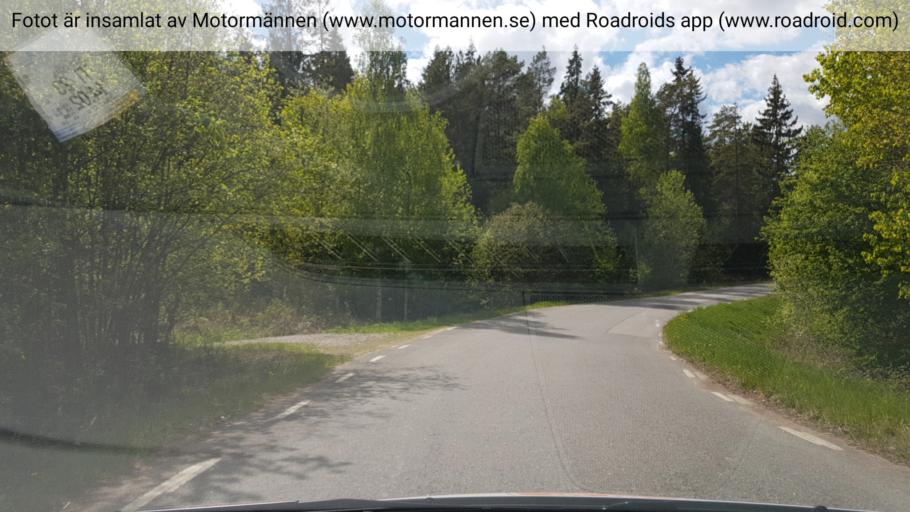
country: SE
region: Kalmar
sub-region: Vasterviks Kommun
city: Forserum
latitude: 57.8585
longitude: 16.5088
